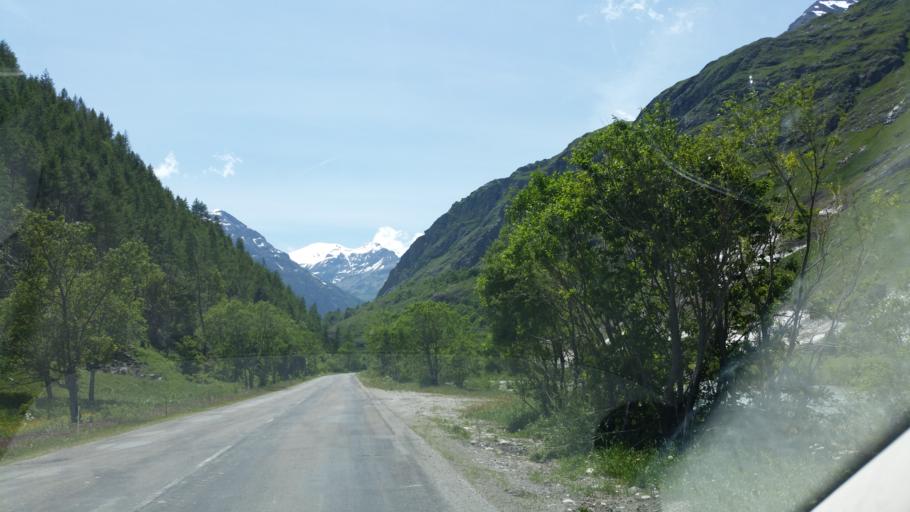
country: FR
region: Rhone-Alpes
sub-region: Departement de la Savoie
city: Val-d'Isere
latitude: 45.3592
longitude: 7.0315
